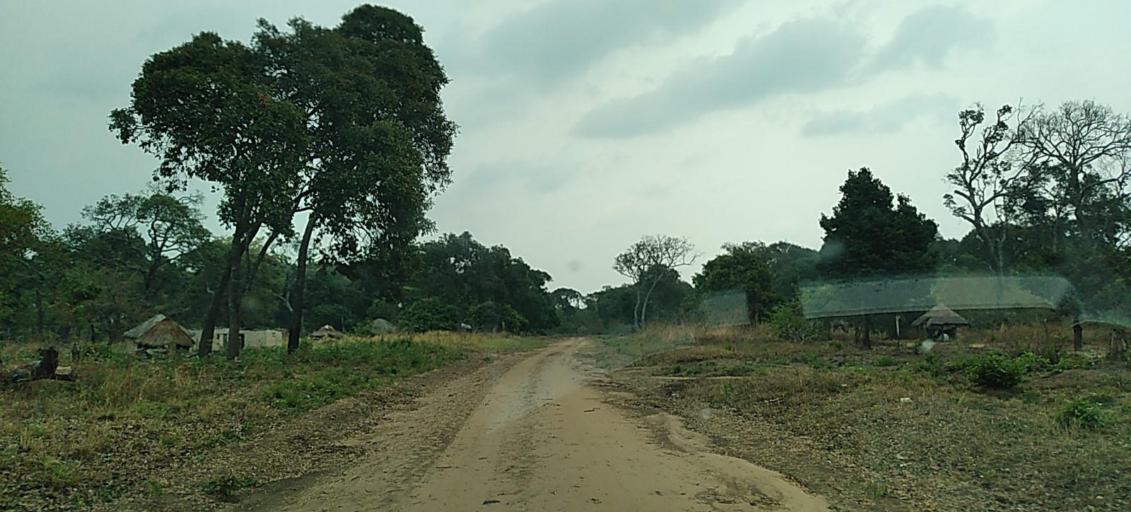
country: ZM
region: North-Western
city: Mwinilunga
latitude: -11.4203
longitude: 24.5977
